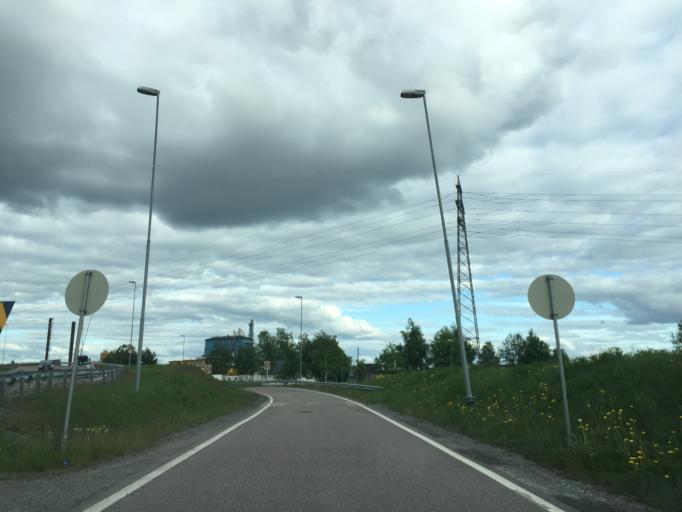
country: NO
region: Akershus
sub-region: Skedsmo
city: Lillestrom
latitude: 59.9478
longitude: 11.0586
